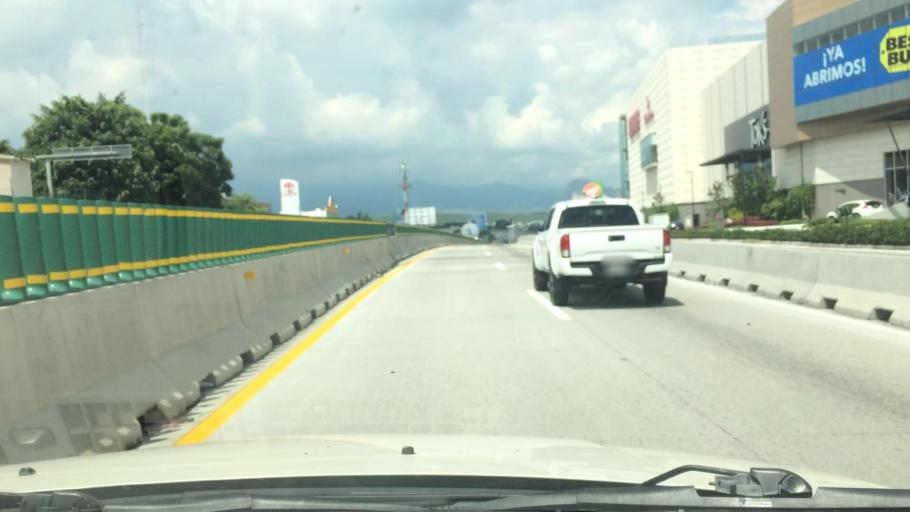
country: MX
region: Morelos
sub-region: Cuernavaca
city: Colonia los Cerritos
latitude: 18.9342
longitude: -99.1981
